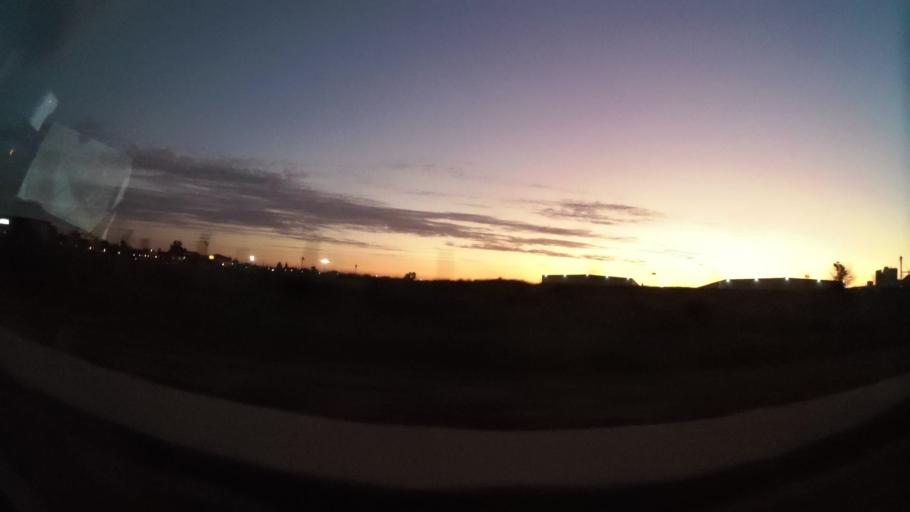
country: AR
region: Buenos Aires
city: Santa Catalina - Dique Lujan
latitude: -34.4589
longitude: -58.7199
